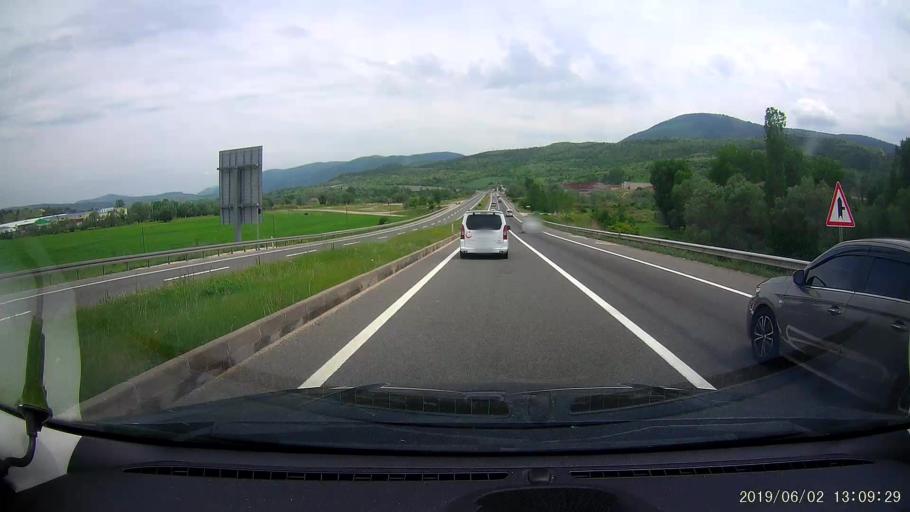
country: TR
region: Karabuk
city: Gozyeri
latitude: 40.8691
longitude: 32.5895
